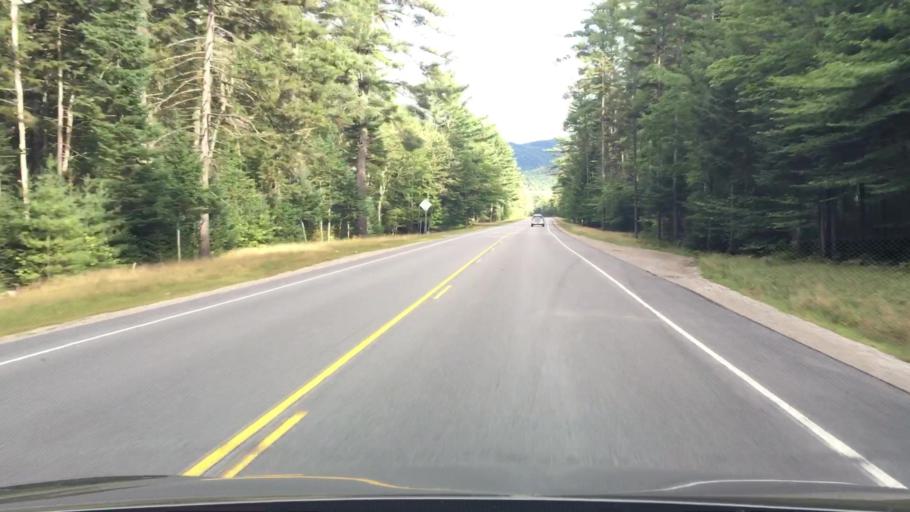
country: US
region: New Hampshire
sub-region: Carroll County
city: Tamworth
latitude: 43.9932
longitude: -71.3286
